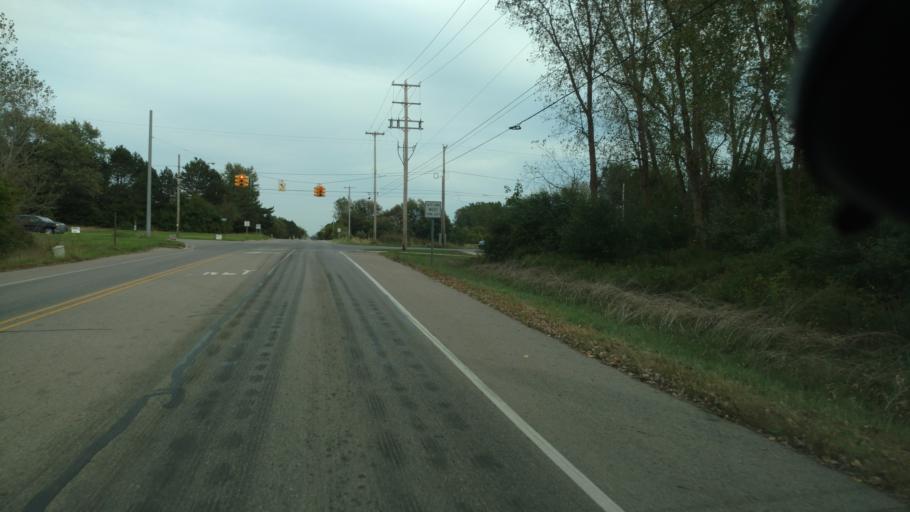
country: US
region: Michigan
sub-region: Ingham County
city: Lansing
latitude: 42.7841
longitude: -84.5239
